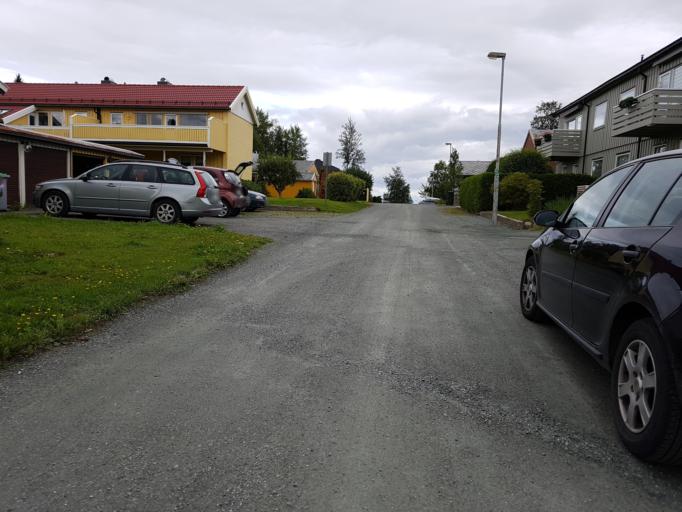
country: NO
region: Sor-Trondelag
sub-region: Trondheim
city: Trondheim
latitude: 63.4065
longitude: 10.4611
